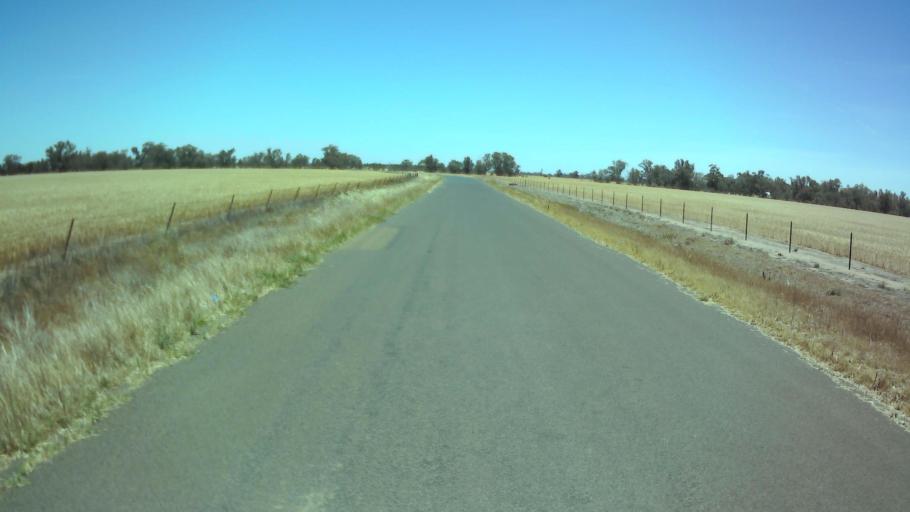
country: AU
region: New South Wales
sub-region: Weddin
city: Grenfell
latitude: -34.0337
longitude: 147.7901
